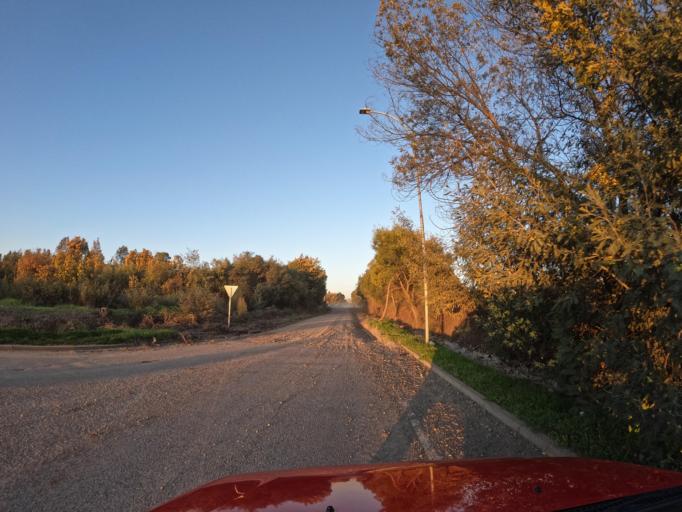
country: CL
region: Biobio
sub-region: Provincia de Nuble
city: San Carlos
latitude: -36.3632
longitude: -71.8778
